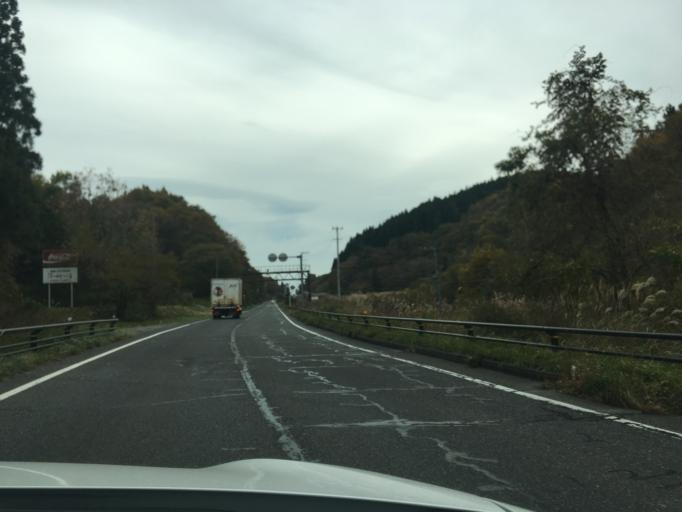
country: JP
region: Fukushima
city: Ishikawa
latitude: 37.2111
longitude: 140.6075
